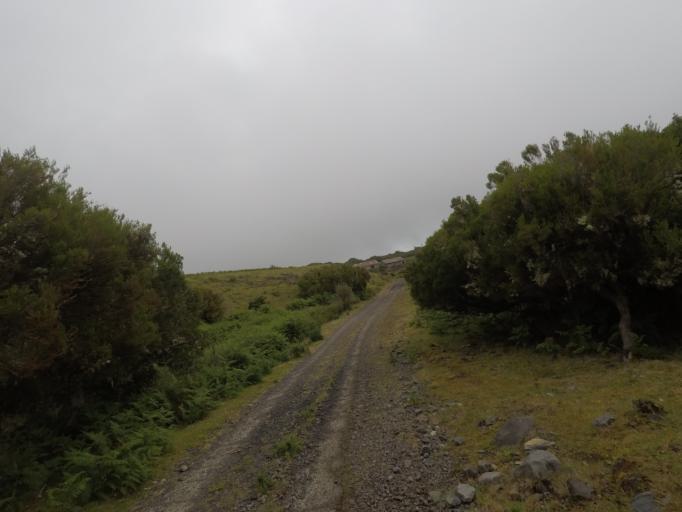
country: PT
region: Madeira
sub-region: Funchal
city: Nossa Senhora do Monte
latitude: 32.7273
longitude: -16.8861
